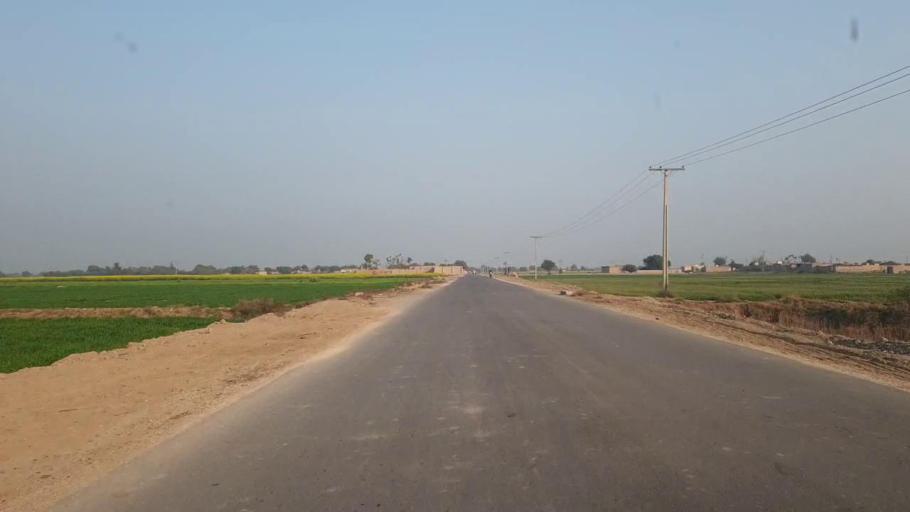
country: PK
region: Sindh
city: Hala
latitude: 25.8103
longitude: 68.4494
